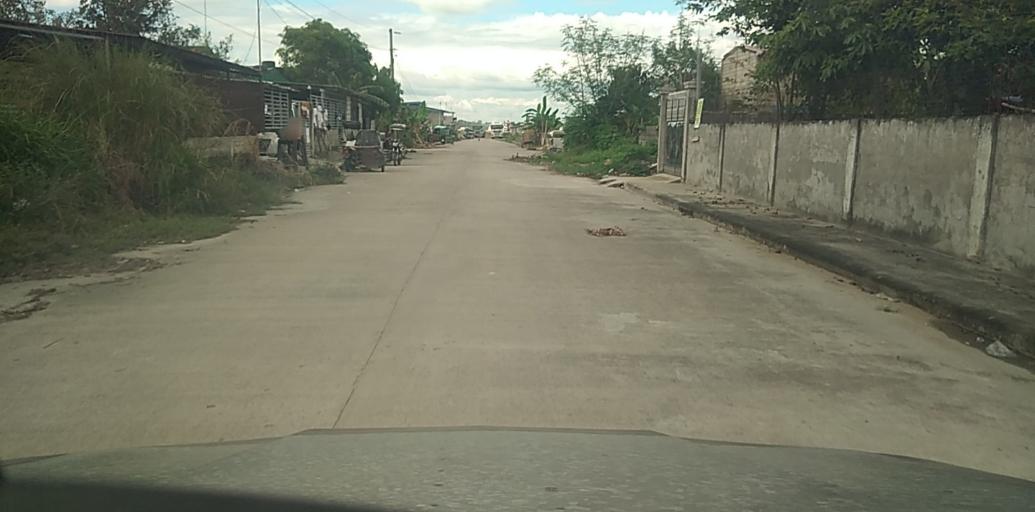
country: PH
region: Central Luzon
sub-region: Province of Pampanga
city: Buensuseso
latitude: 15.1811
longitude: 120.6664
